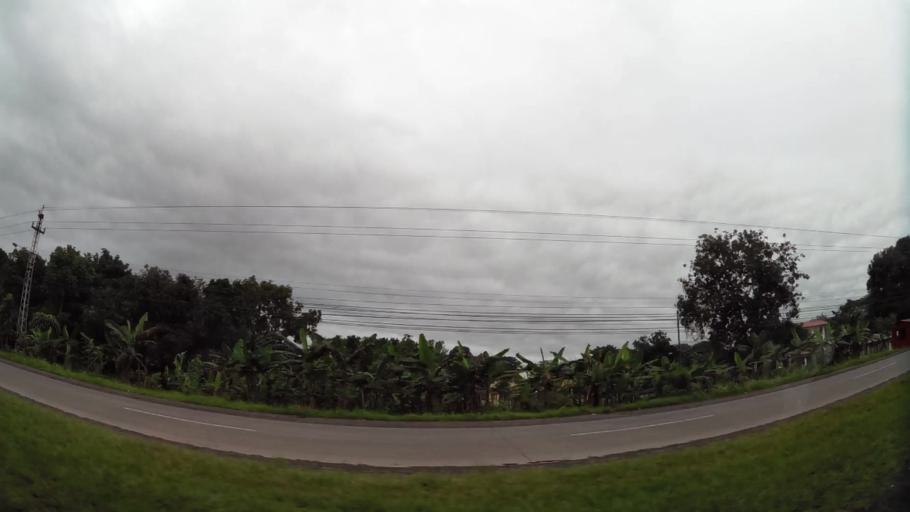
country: PA
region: Chiriqui
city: Tijera
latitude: 8.4703
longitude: -82.5348
